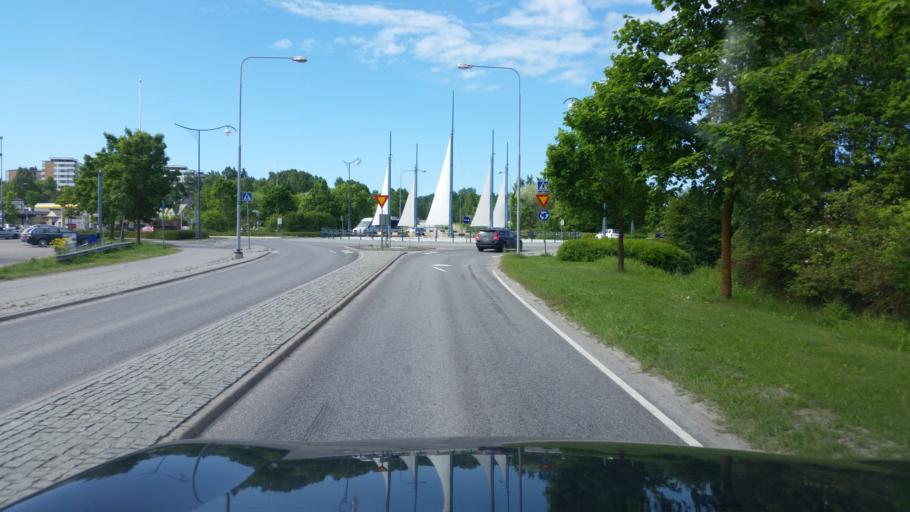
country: FI
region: Varsinais-Suomi
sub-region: Aboland-Turunmaa
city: Pargas
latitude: 60.3071
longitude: 22.3020
